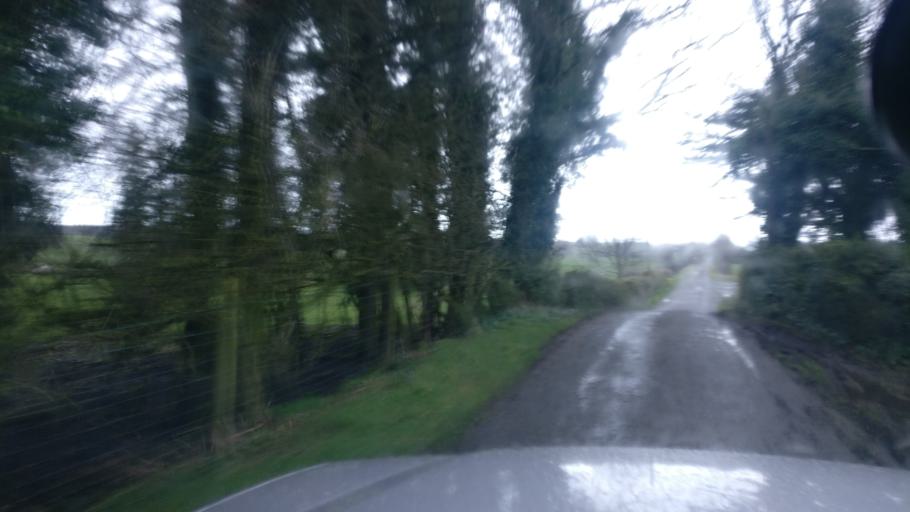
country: IE
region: Connaught
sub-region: County Galway
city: Loughrea
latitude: 53.2469
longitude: -8.4267
